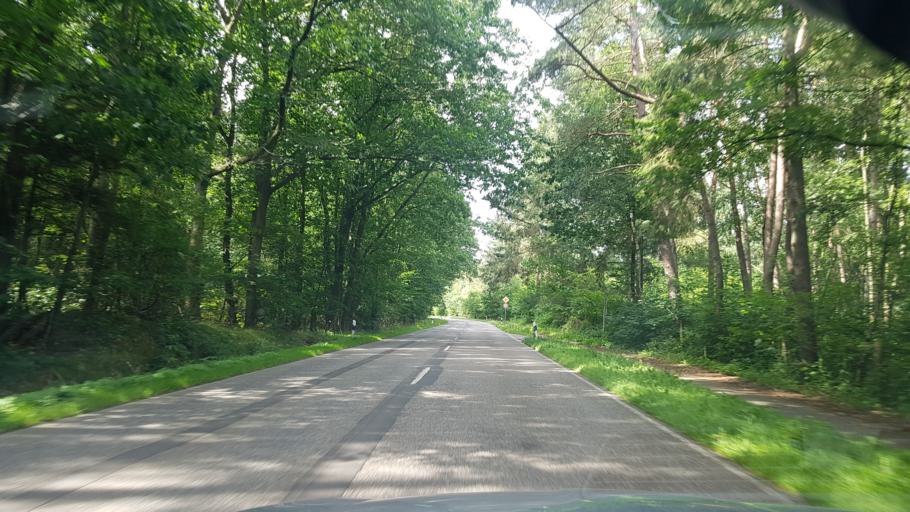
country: DE
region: Schleswig-Holstein
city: Bramstedtlund
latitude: 54.8594
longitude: 9.0441
